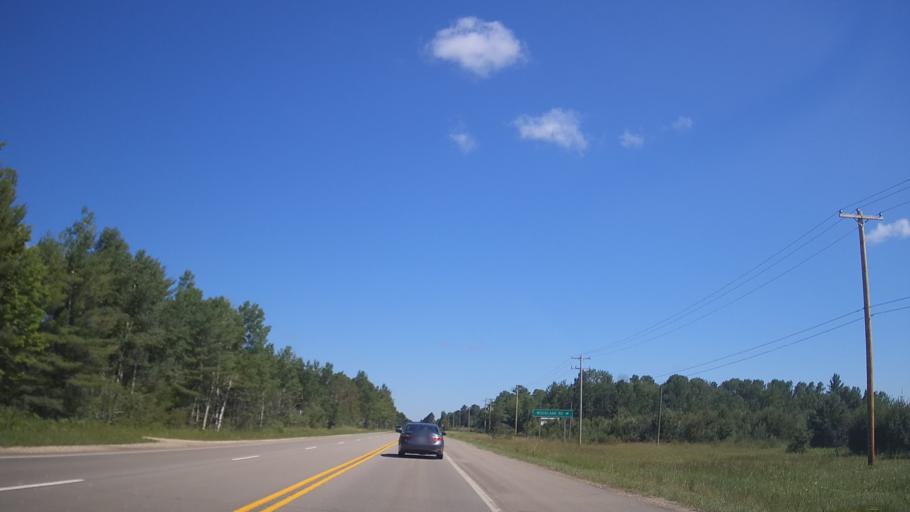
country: US
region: Michigan
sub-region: Cheboygan County
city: Indian River
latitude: 45.5266
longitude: -84.7818
